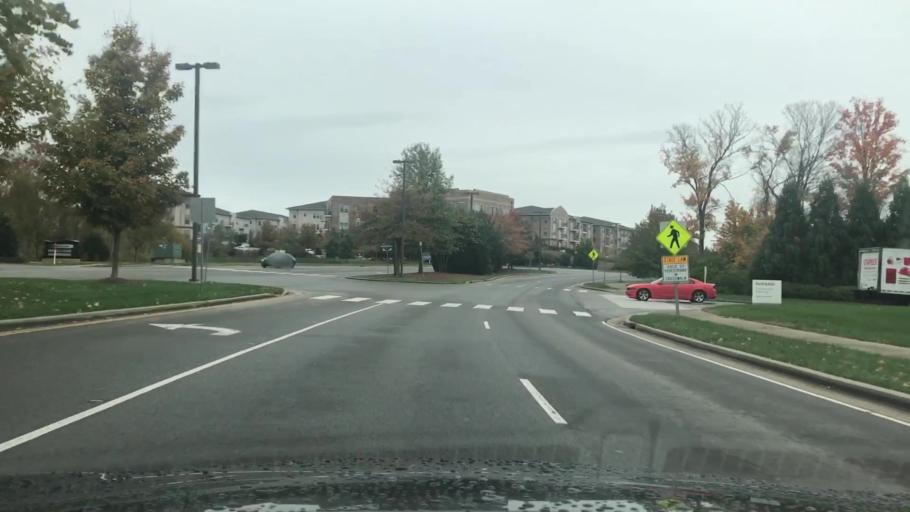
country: US
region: Tennessee
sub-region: Williamson County
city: Franklin
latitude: 35.9388
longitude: -86.8099
